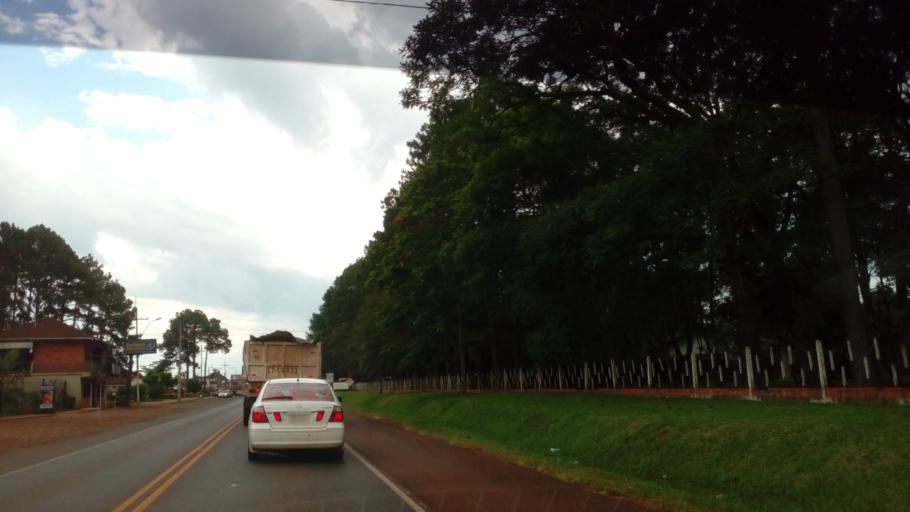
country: PY
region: Itapua
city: Obligado
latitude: -27.0755
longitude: -55.6420
